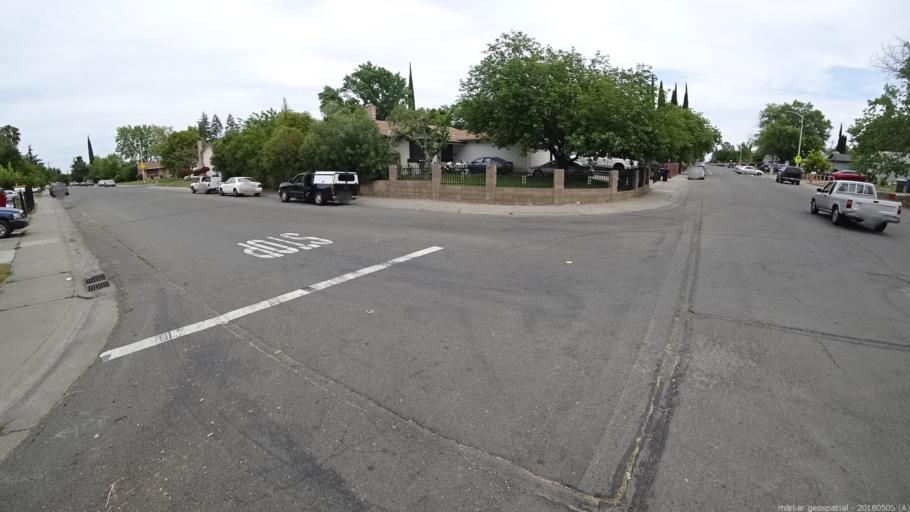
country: US
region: California
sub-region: Sacramento County
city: Rio Linda
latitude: 38.6478
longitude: -121.4658
